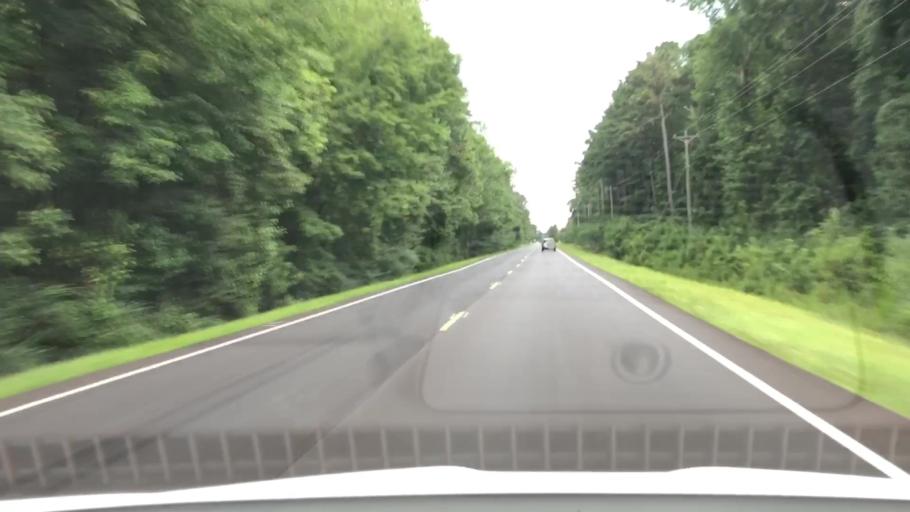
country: US
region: North Carolina
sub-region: Jones County
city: Maysville
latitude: 34.8738
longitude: -77.1988
